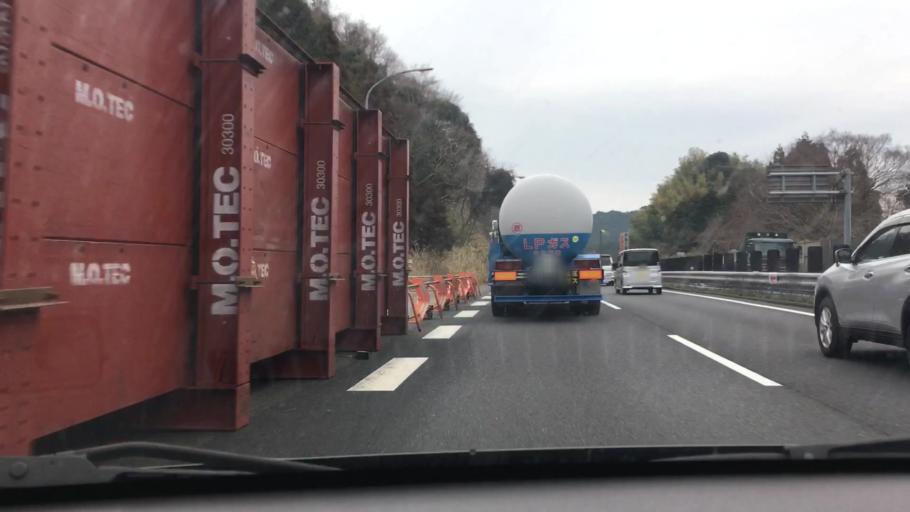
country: JP
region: Mie
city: Kameyama
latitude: 34.8416
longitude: 136.3678
